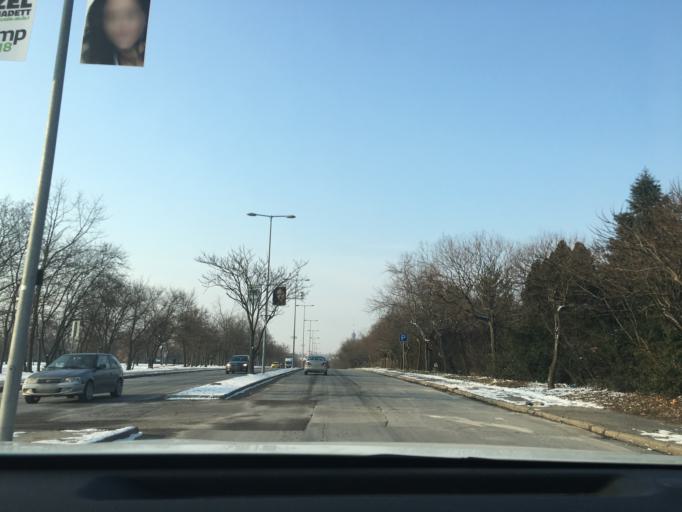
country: HU
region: Budapest
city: Budapest X. keruelet
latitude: 47.4830
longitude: 19.1450
